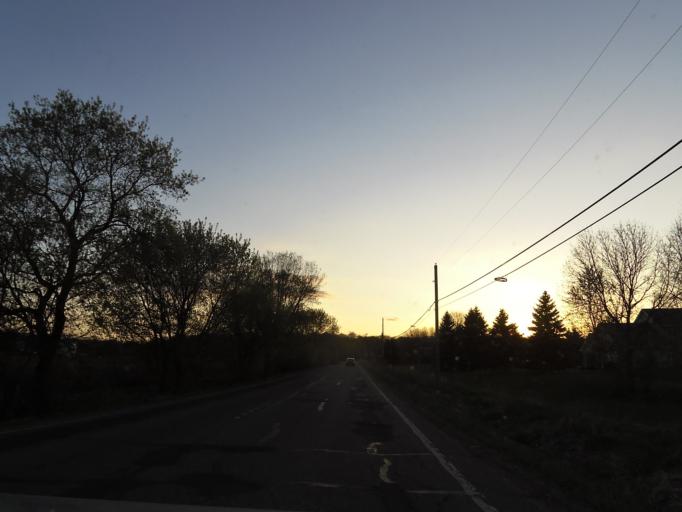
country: US
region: Wisconsin
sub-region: Saint Croix County
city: Hudson
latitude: 44.9802
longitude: -92.7869
